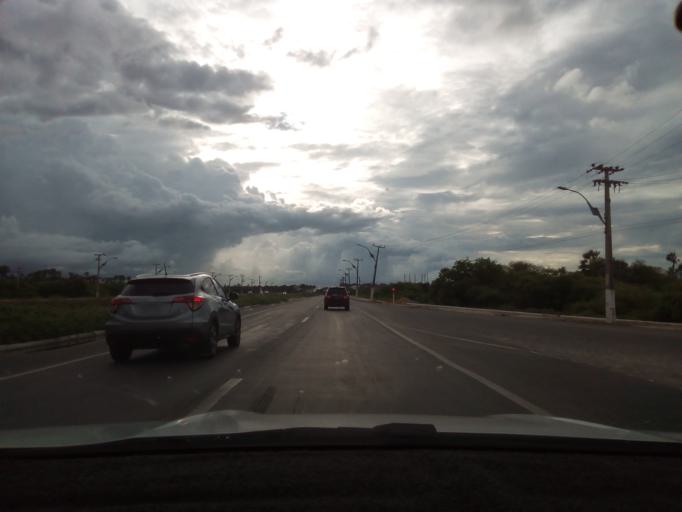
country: BR
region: Ceara
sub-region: Aracati
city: Aracati
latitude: -4.5786
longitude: -37.7803
